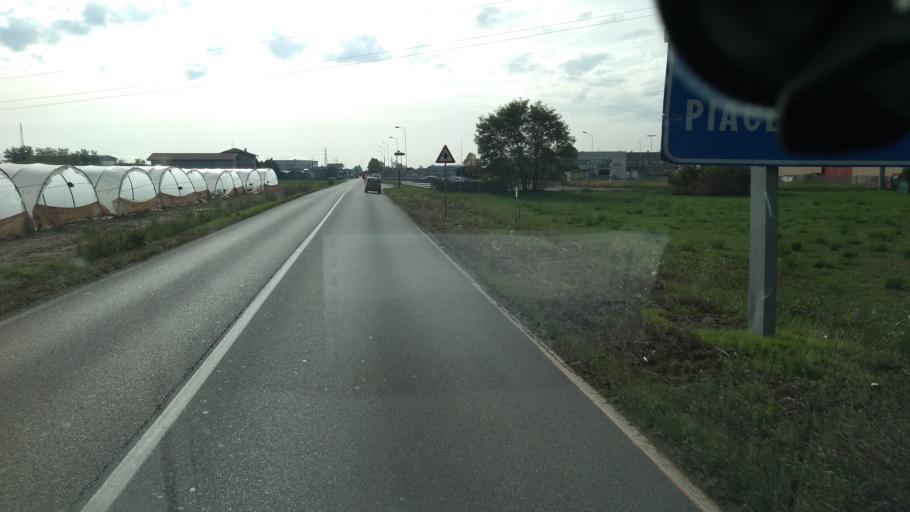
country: IT
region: Lombardy
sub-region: Provincia di Bergamo
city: Zanica
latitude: 45.6255
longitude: 9.6893
